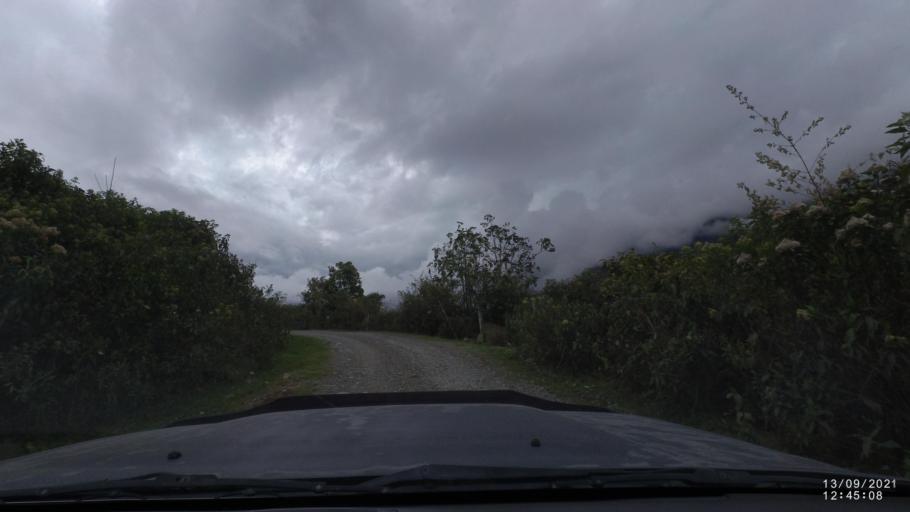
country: BO
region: Cochabamba
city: Colomi
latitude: -17.2488
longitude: -65.8172
